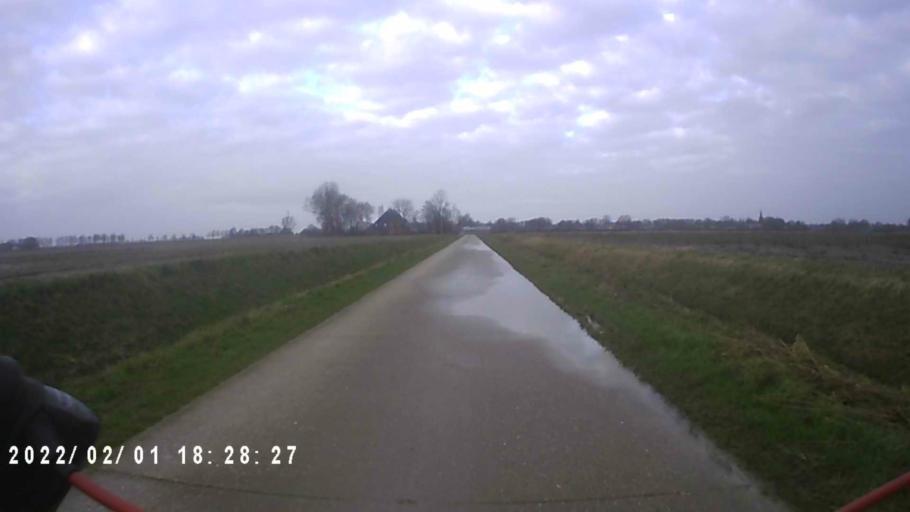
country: NL
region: Groningen
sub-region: Gemeente De Marne
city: Ulrum
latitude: 53.3518
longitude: 6.3193
